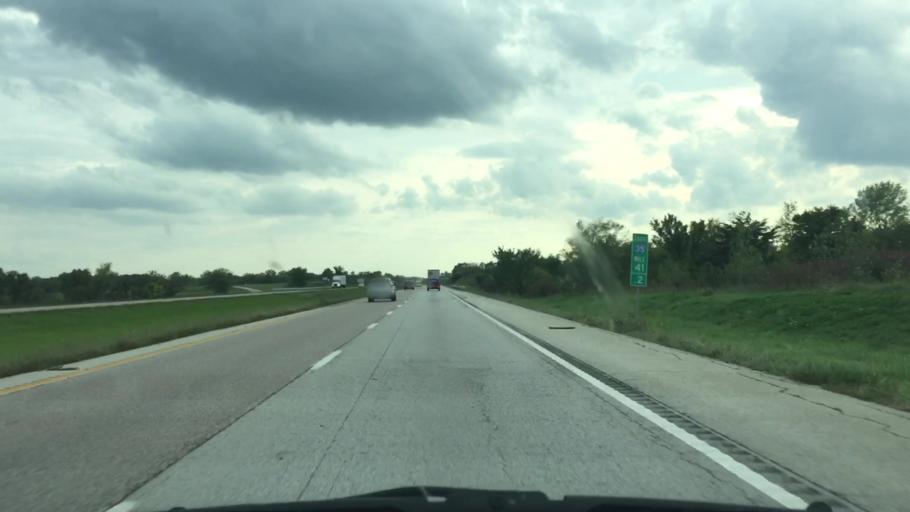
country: US
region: Missouri
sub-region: Clinton County
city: Lathrop
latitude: 39.5685
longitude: -94.2633
